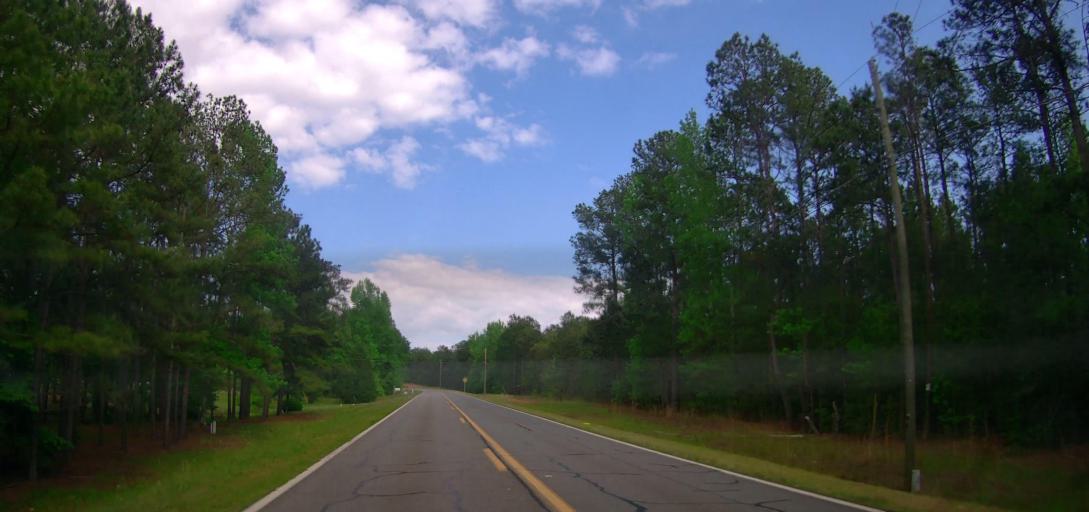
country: US
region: Georgia
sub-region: Baldwin County
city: Hardwick
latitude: 33.0625
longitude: -83.1554
